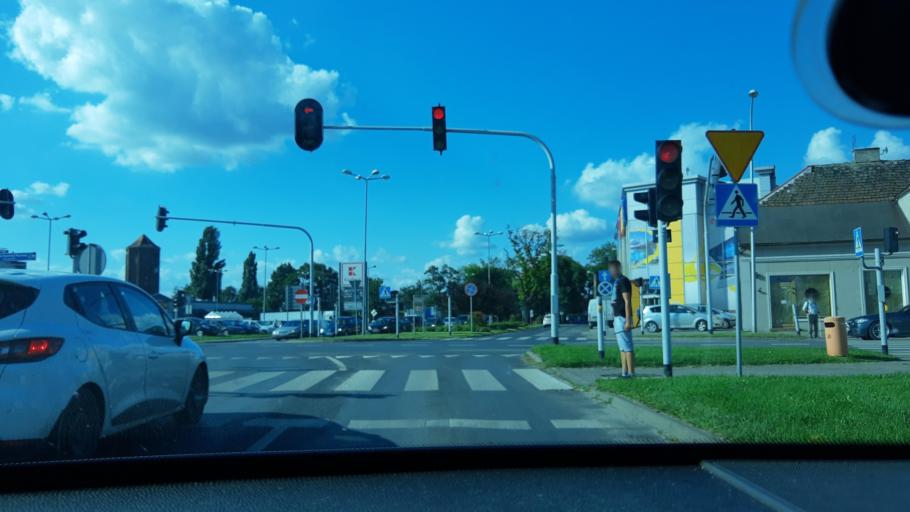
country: PL
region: Lodz Voivodeship
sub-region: Powiat sieradzki
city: Sieradz
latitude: 51.5953
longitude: 18.7152
